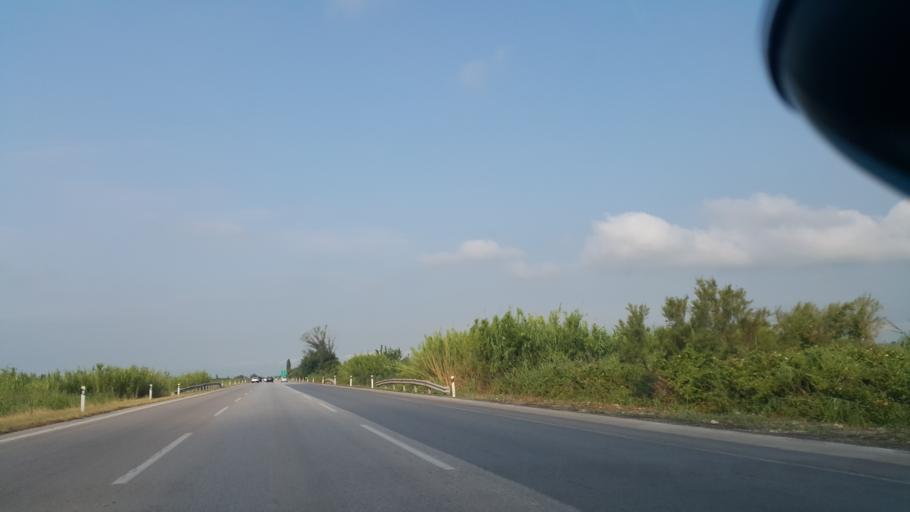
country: GR
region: Central Macedonia
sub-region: Nomos Thessalonikis
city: Chalastra
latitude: 40.6298
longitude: 22.7736
